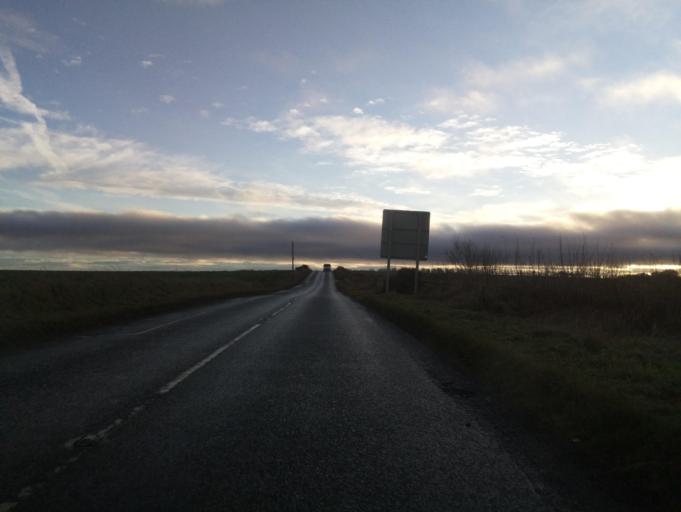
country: GB
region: Scotland
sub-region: Angus
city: Letham
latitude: 56.5768
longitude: -2.7799
